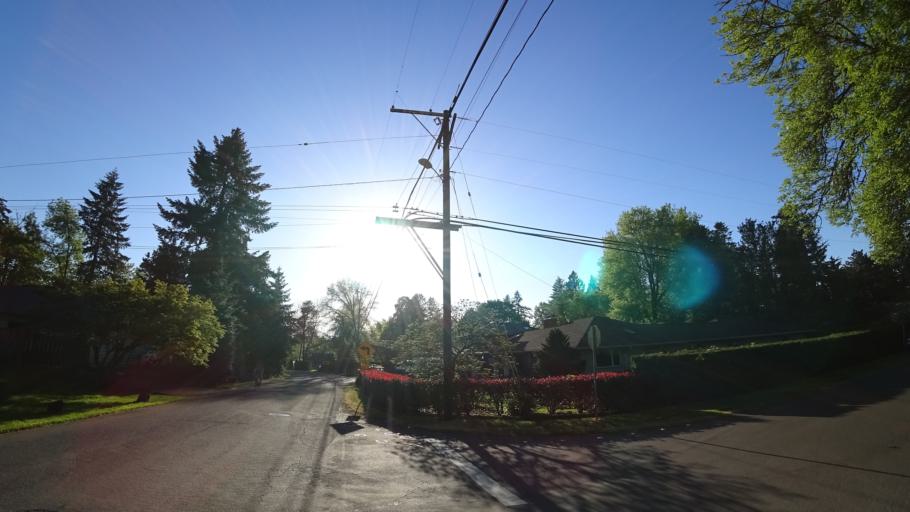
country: US
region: Oregon
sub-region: Washington County
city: Raleigh Hills
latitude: 45.4882
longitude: -122.7672
